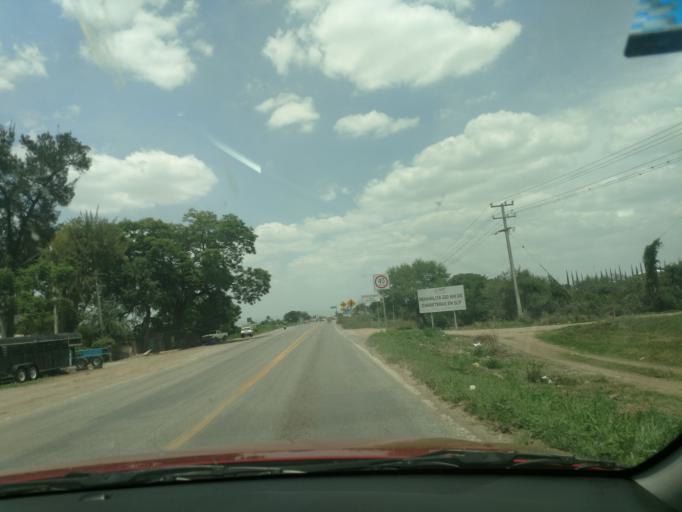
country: MX
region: San Luis Potosi
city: Ciudad Fernandez
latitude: 21.9429
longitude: -100.0446
